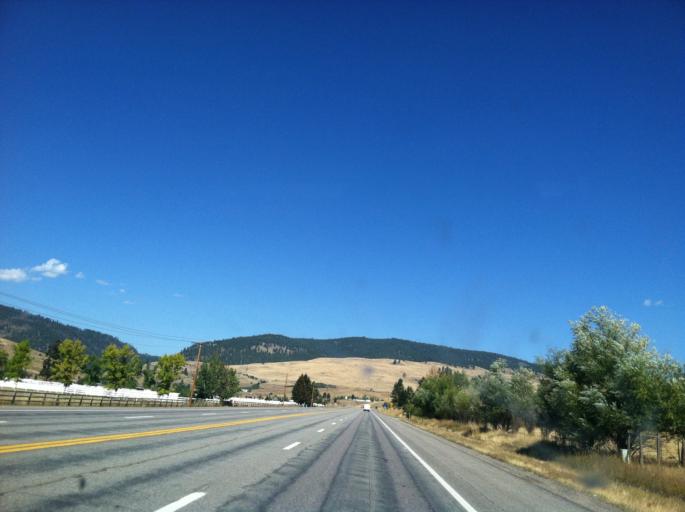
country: US
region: Montana
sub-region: Missoula County
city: Frenchtown
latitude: 46.9714
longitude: -114.1296
